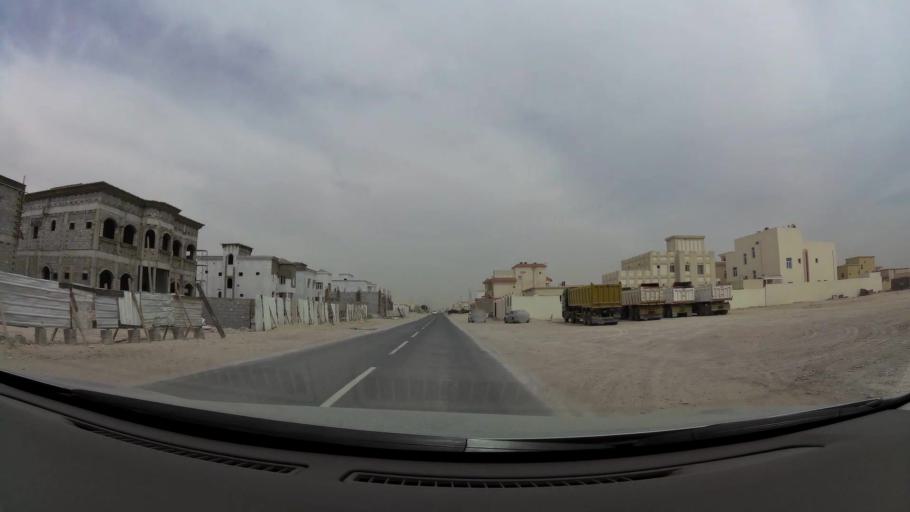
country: QA
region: Baladiyat ar Rayyan
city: Ar Rayyan
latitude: 25.2182
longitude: 51.4634
